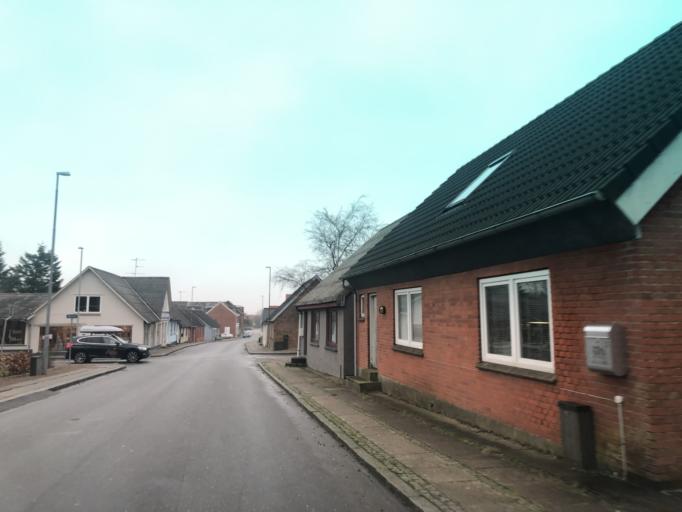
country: DK
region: North Denmark
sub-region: Thisted Kommune
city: Hurup
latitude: 56.7474
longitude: 8.4202
